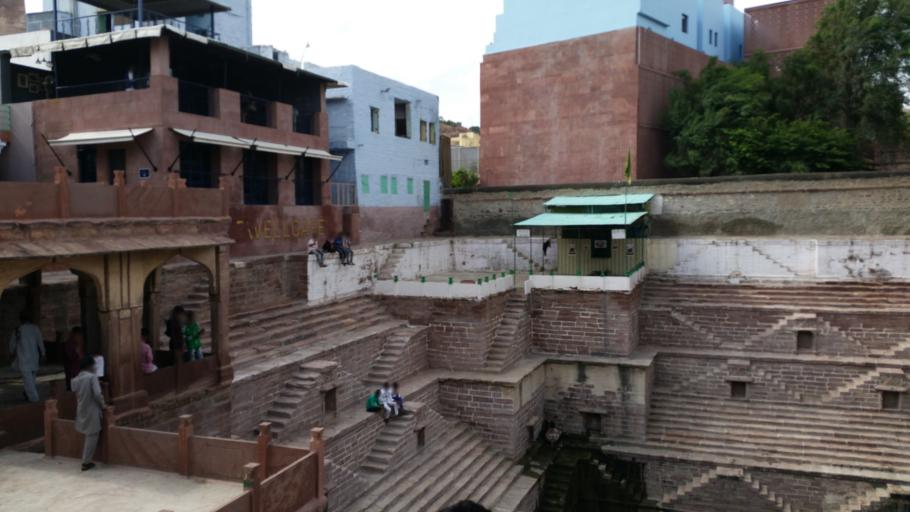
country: IN
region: Rajasthan
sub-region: Jodhpur
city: Jodhpur
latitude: 26.2970
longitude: 73.0230
